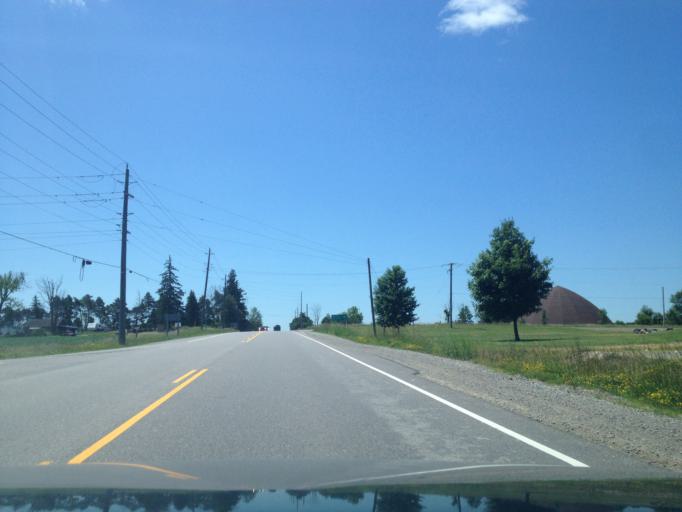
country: CA
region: Ontario
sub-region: Wellington County
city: Guelph
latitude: 43.6203
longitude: -80.0952
